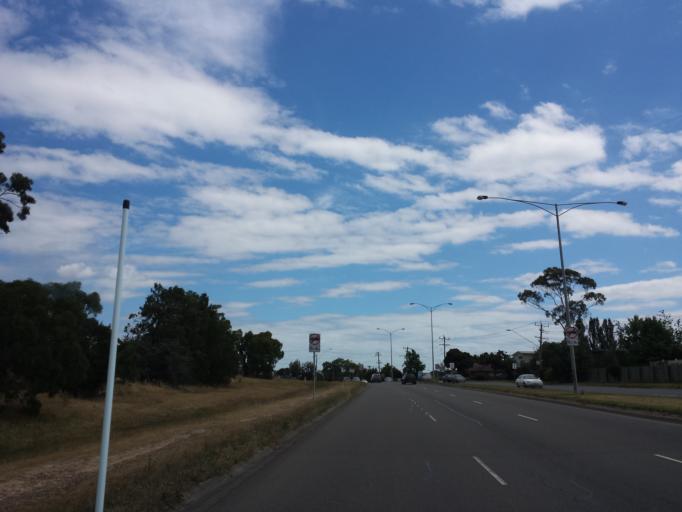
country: AU
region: Victoria
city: Watsonia
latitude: -37.7153
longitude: 145.0825
